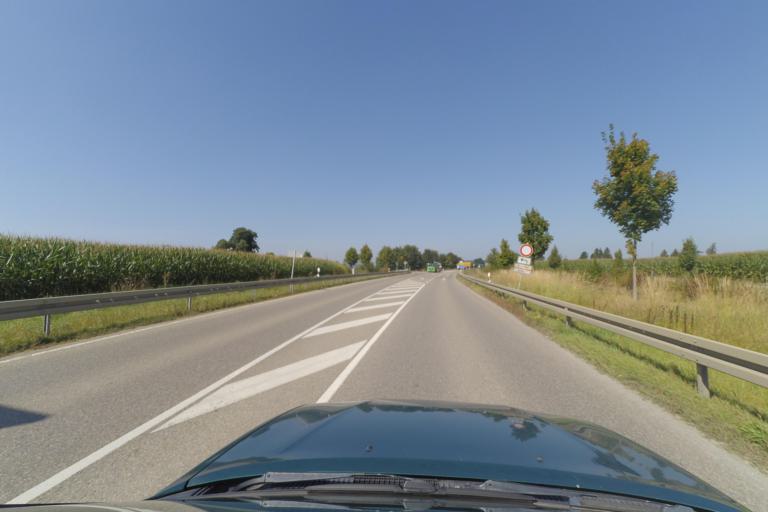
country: DE
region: Bavaria
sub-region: Swabia
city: Lauingen
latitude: 48.5788
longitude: 10.4102
